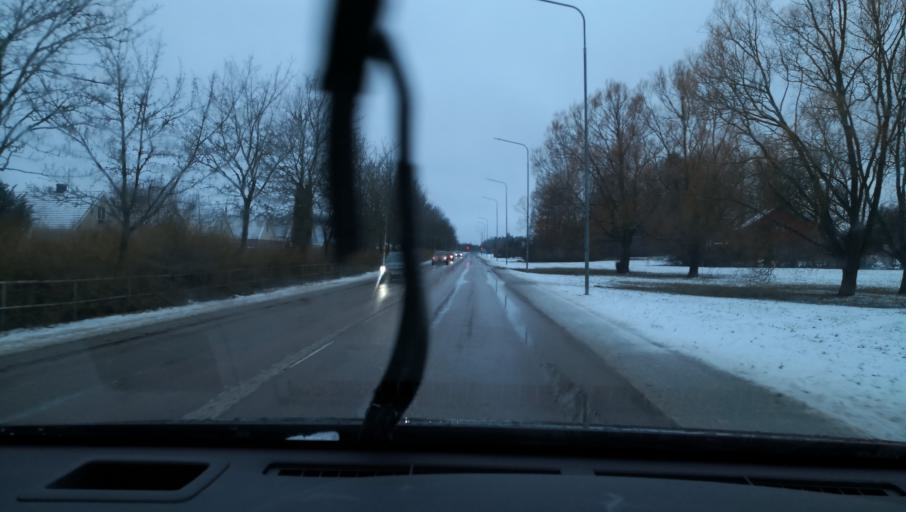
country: SE
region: Vaestmanland
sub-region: Kopings Kommun
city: Koping
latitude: 59.5174
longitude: 16.0106
